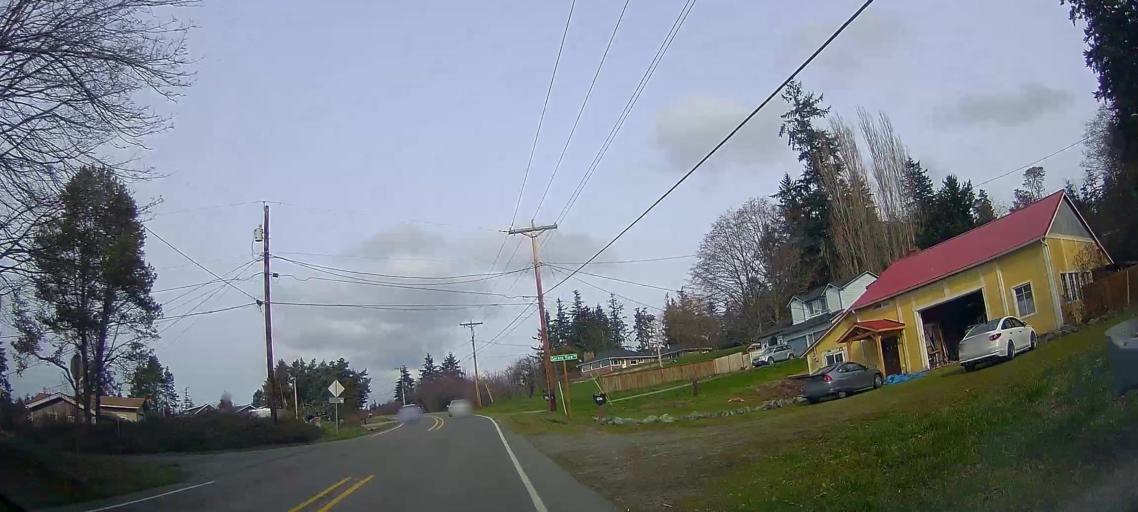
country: US
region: Washington
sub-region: Island County
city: Camano
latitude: 48.1762
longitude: -122.5277
